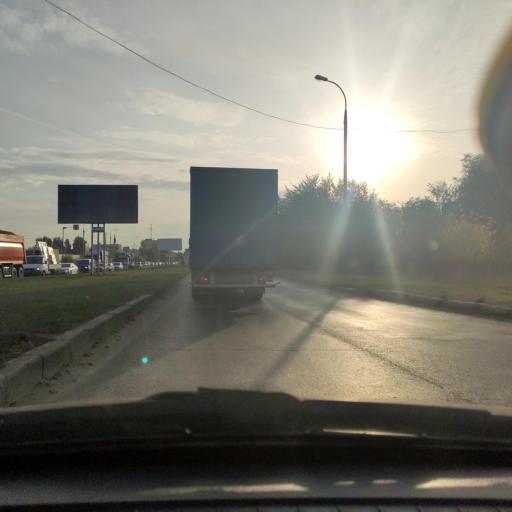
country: RU
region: Samara
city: Tol'yatti
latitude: 53.5611
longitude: 49.2900
